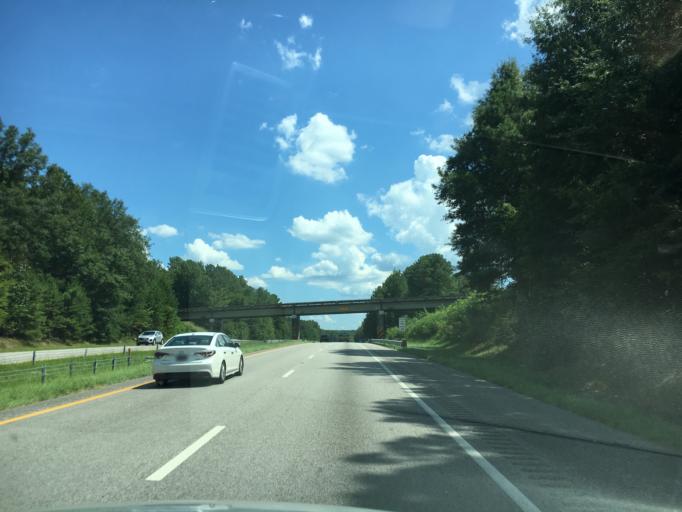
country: US
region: South Carolina
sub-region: Laurens County
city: Clinton
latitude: 34.5237
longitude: -81.8778
